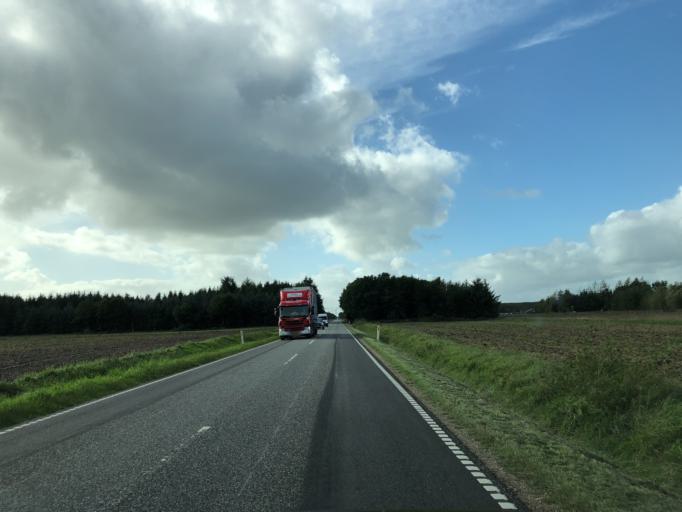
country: DK
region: Central Jutland
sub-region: Holstebro Kommune
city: Holstebro
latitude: 56.3697
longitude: 8.5603
